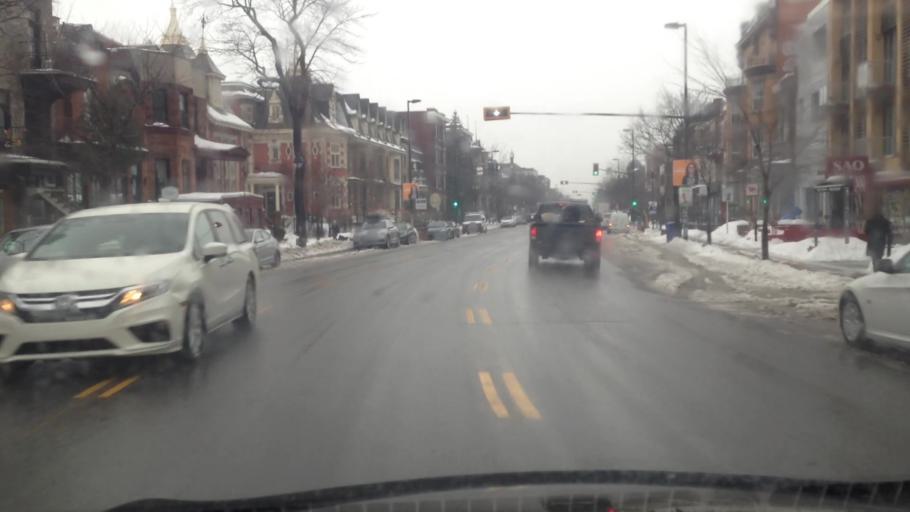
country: CA
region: Quebec
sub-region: Montreal
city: Montreal
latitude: 45.5207
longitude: -73.5988
